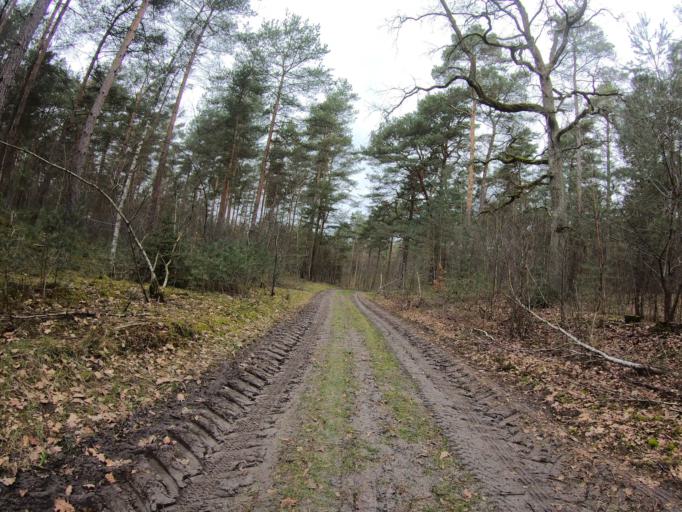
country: DE
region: Lower Saxony
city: Leiferde
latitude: 52.4855
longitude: 10.4502
